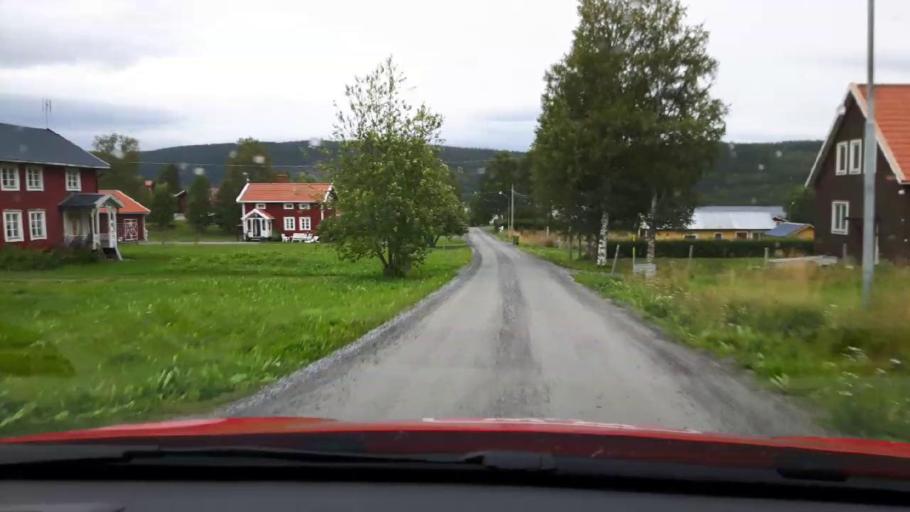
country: SE
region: Jaemtland
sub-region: Are Kommun
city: Are
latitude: 63.4922
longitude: 13.1216
